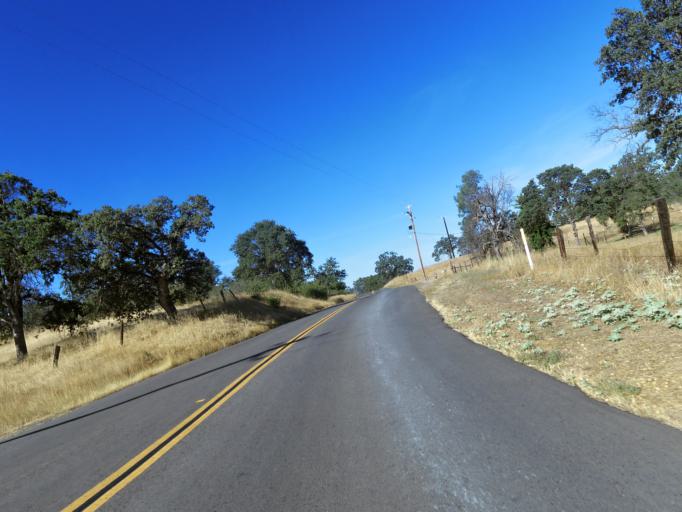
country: US
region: California
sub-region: Madera County
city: Yosemite Lakes
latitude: 37.1924
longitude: -119.8150
